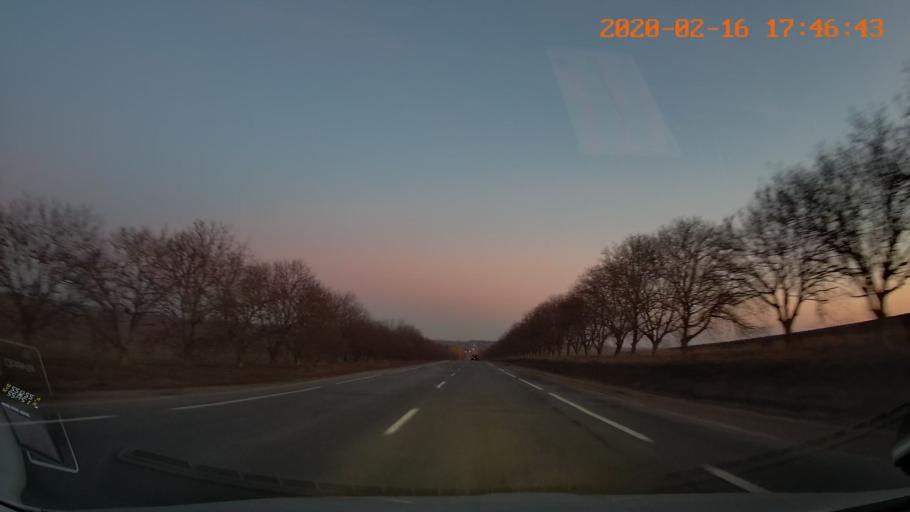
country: MD
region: Riscani
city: Riscani
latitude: 47.9673
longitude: 27.5969
